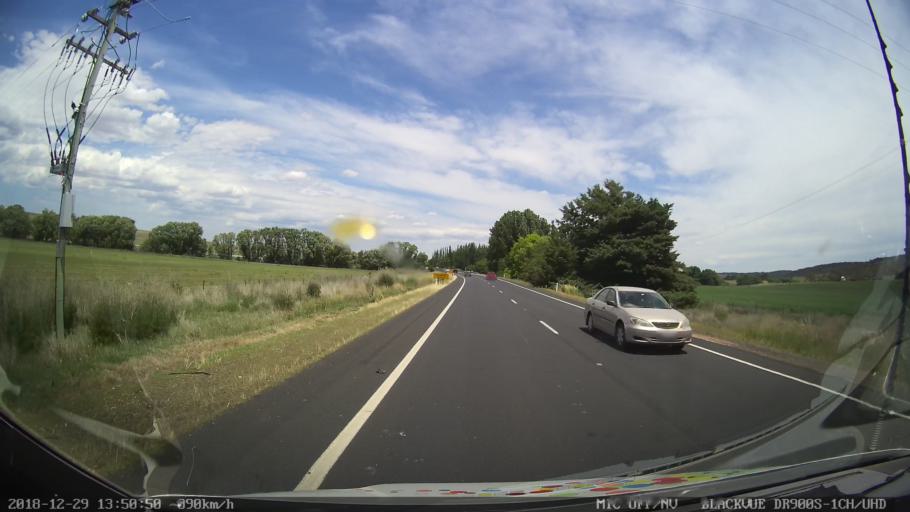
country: AU
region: New South Wales
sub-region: Cooma-Monaro
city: Cooma
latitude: -36.1733
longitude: 149.1541
